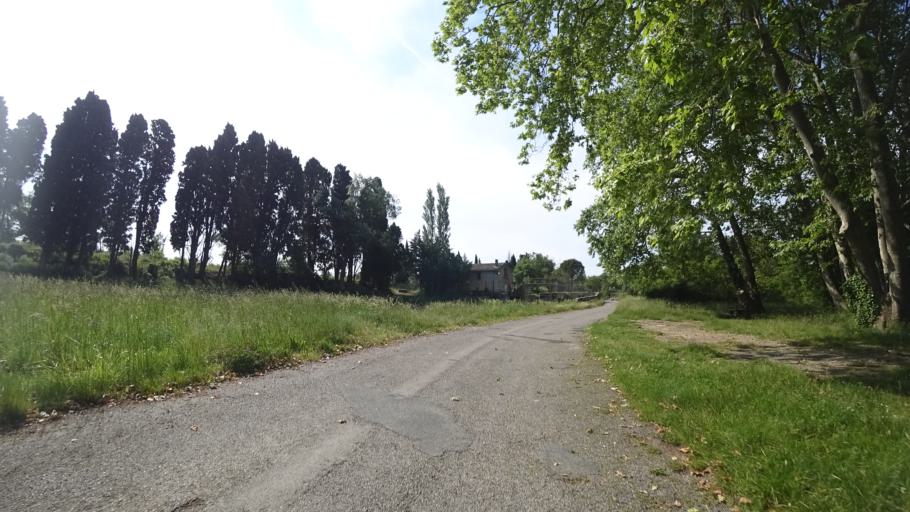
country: FR
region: Languedoc-Roussillon
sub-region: Departement de l'Herault
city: Olonzac
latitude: 43.2685
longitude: 2.7398
